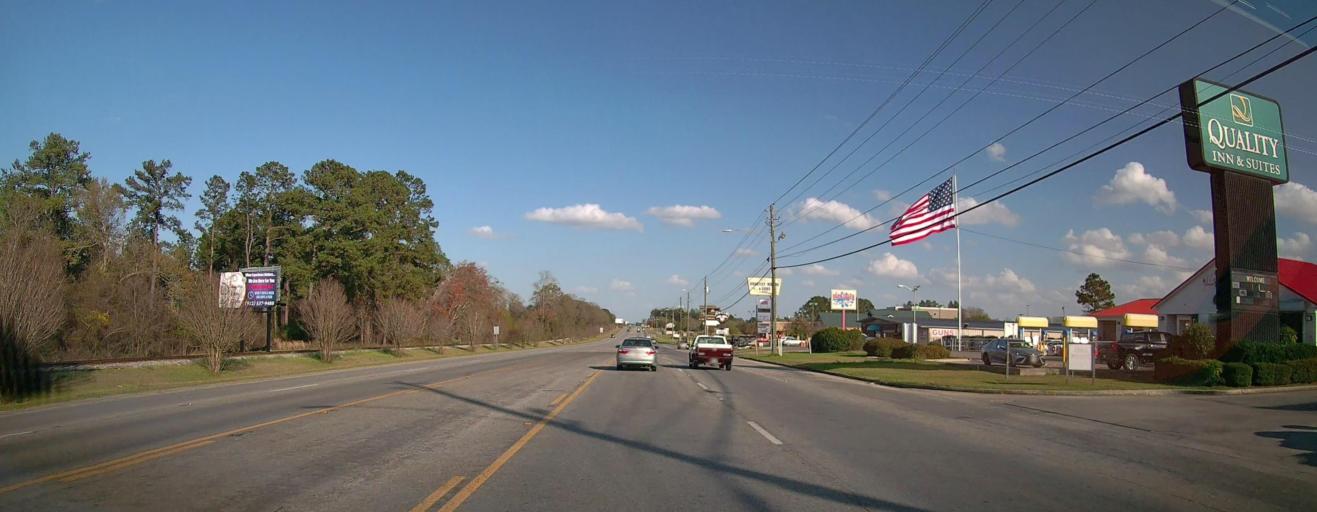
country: US
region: Georgia
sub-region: Toombs County
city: Vidalia
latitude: 32.2065
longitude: -82.3735
